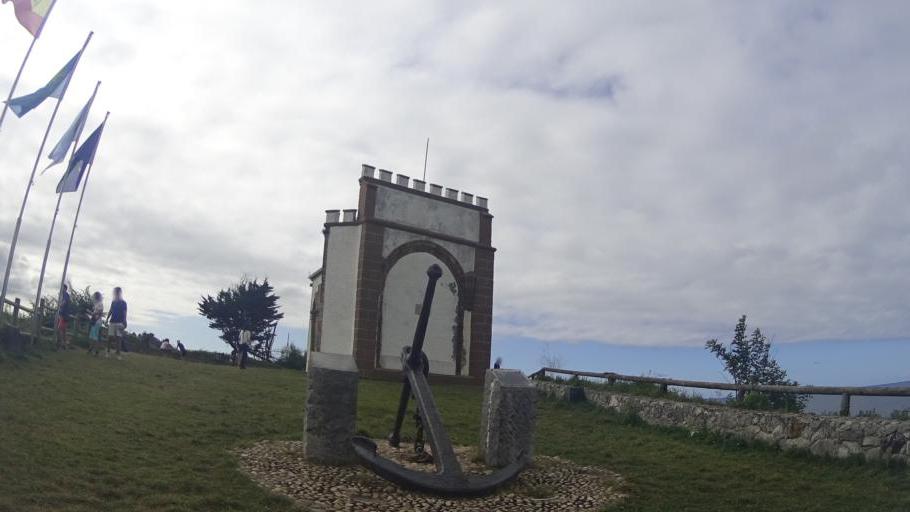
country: ES
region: Asturias
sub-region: Province of Asturias
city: Ribadesella
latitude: 43.4683
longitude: -5.0645
